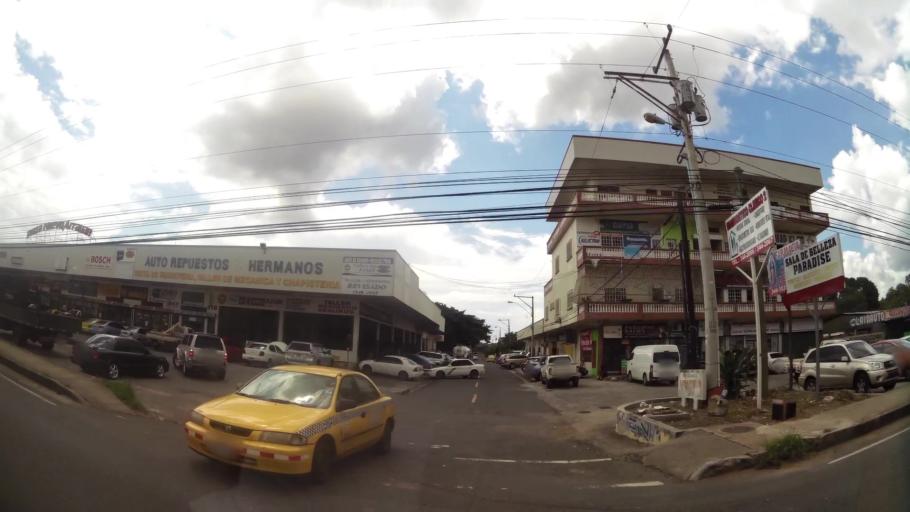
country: PA
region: Panama
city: Nuevo Arraijan
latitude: 8.9271
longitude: -79.7254
